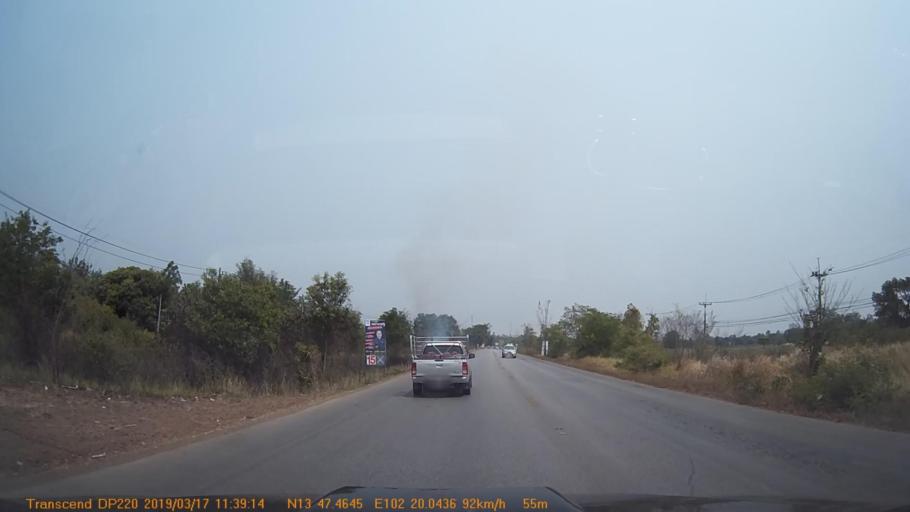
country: TH
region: Sa Kaeo
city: Watthana Nakhon
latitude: 13.7915
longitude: 102.3342
